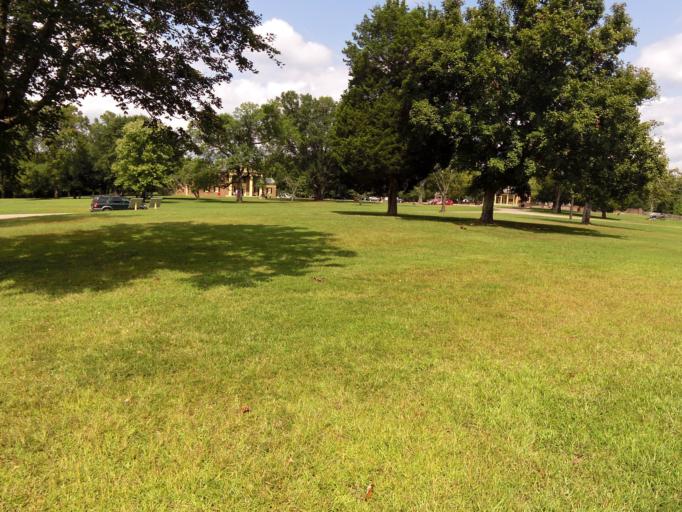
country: US
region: Tennessee
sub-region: Hardin County
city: Crump
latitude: 35.1502
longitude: -88.3232
